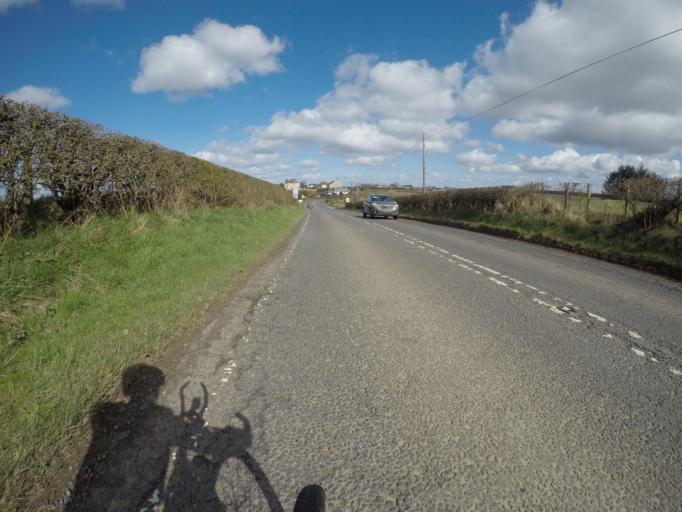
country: GB
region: Scotland
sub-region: East Ayrshire
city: Crosshouse
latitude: 55.5911
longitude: -4.5540
